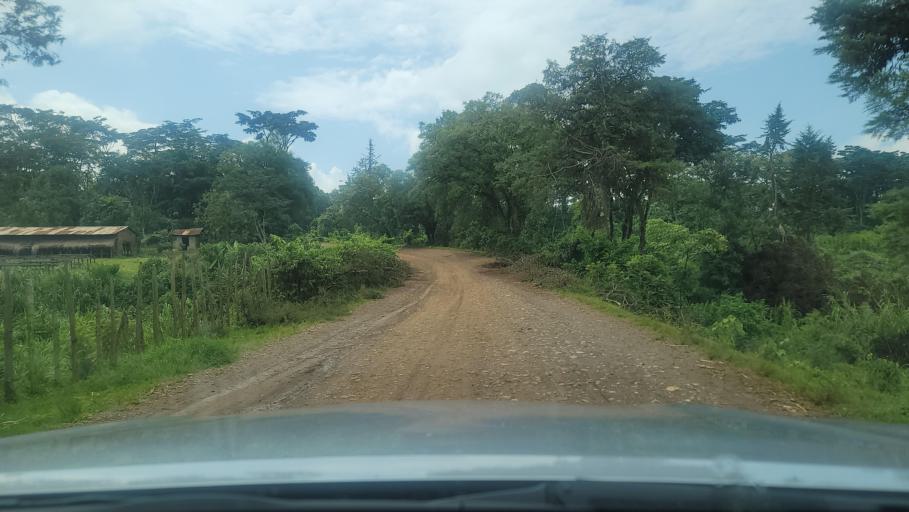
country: ET
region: Oromiya
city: Agaro
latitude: 7.7909
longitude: 36.4332
